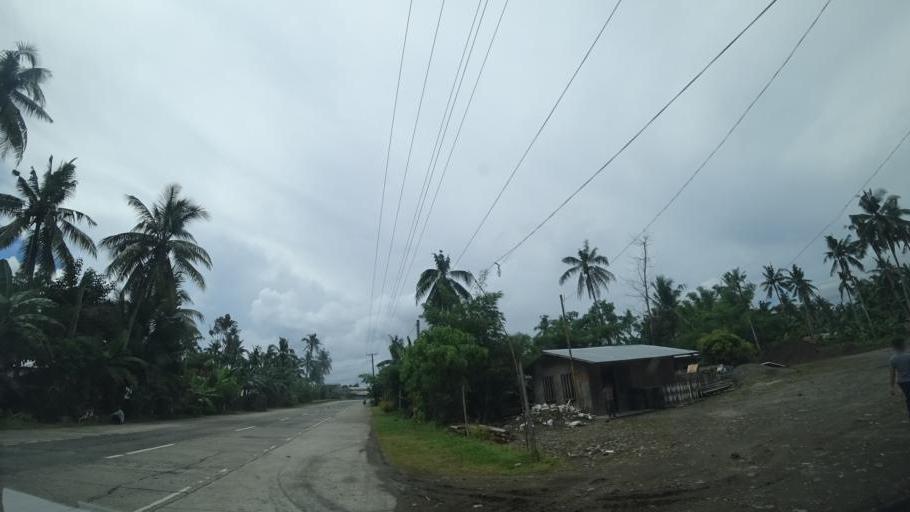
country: PH
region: Eastern Visayas
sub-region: Province of Leyte
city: MacArthur
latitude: 10.8536
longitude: 124.9950
